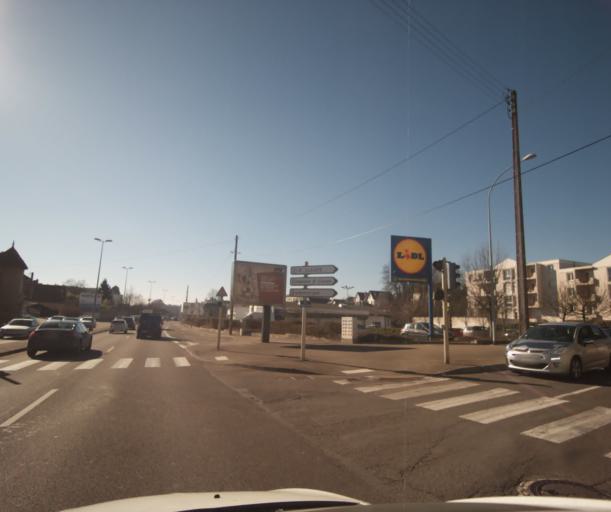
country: FR
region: Franche-Comte
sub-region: Departement du Doubs
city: Besancon
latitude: 47.2561
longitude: 6.0202
